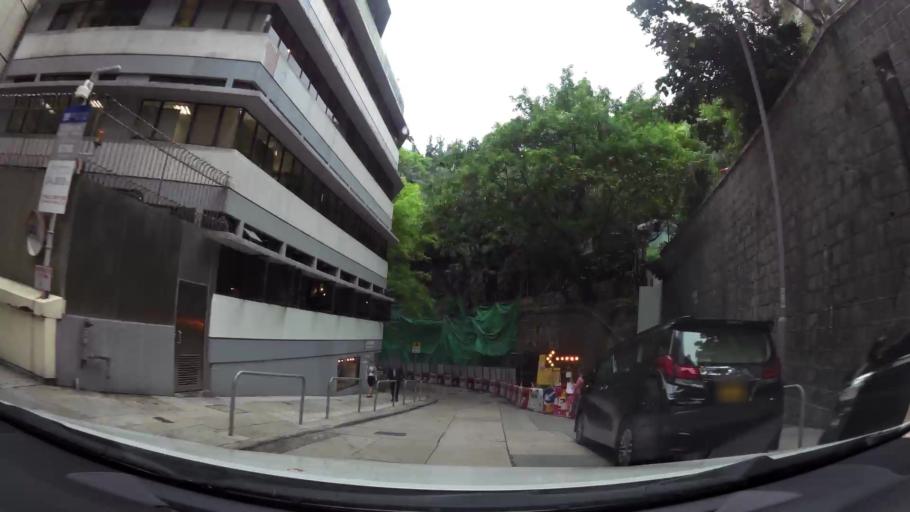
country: HK
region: Central and Western
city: Central
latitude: 22.2804
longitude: 114.1564
